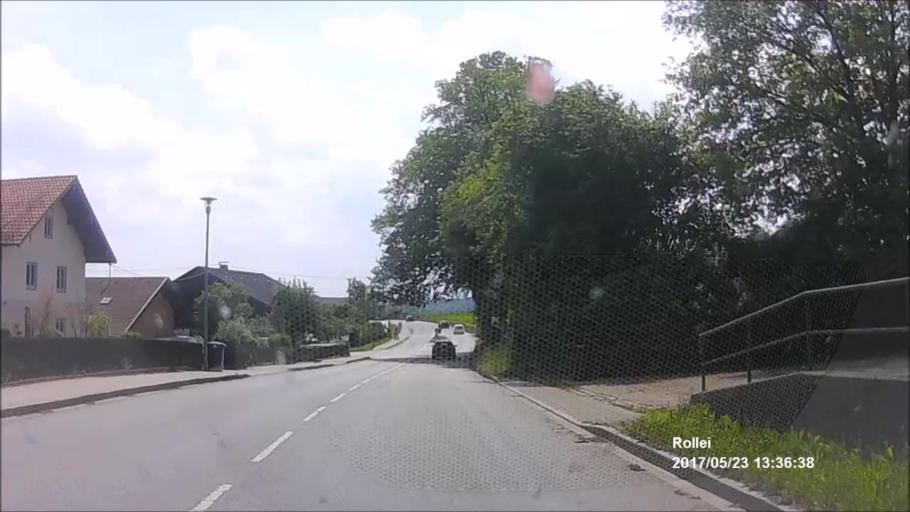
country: DE
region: Bavaria
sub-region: Upper Bavaria
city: Dorfen
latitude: 48.2508
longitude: 12.1600
